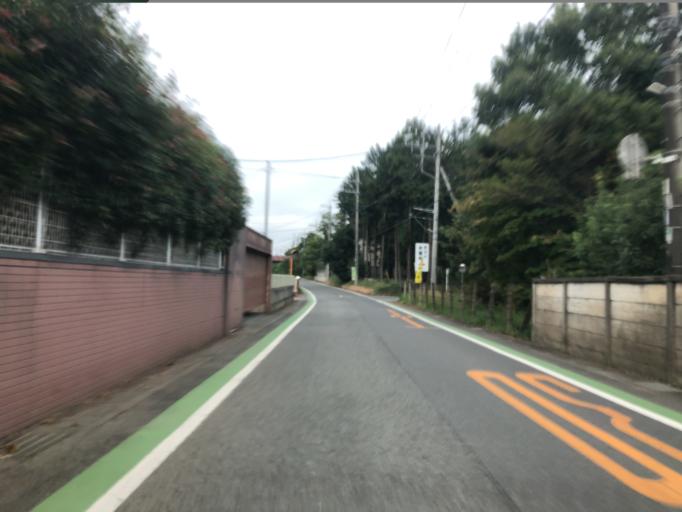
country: JP
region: Saitama
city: Fukiage-fujimi
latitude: 36.0550
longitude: 139.3914
